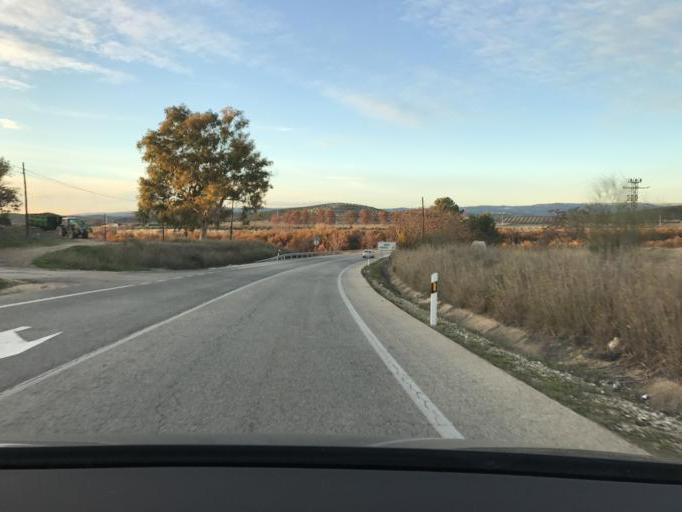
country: ES
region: Andalusia
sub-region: Provincia de Jaen
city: Jodar
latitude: 37.9164
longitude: -3.3489
